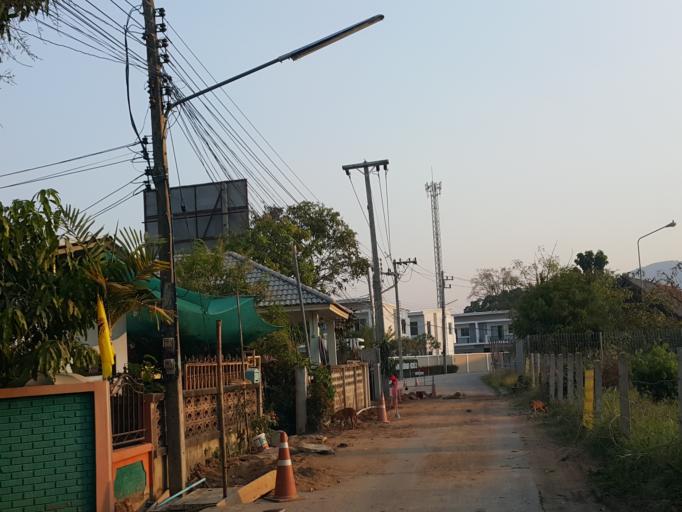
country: TH
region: Chiang Mai
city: San Sai
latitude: 18.8999
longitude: 98.9534
